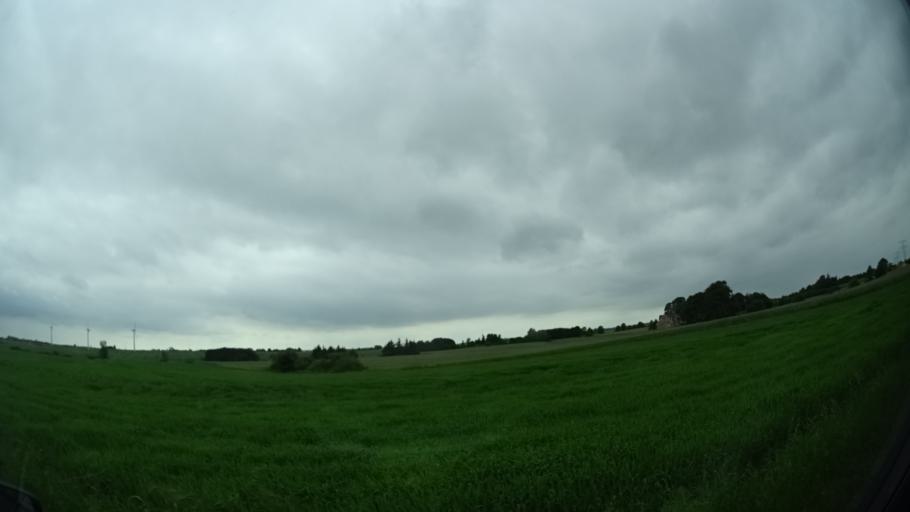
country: DK
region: Central Jutland
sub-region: Arhus Kommune
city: Kolt
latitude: 56.0790
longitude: 10.0859
